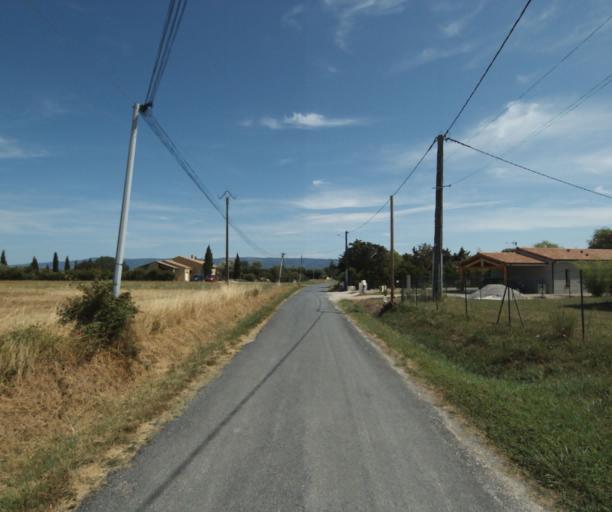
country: FR
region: Midi-Pyrenees
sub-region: Departement du Tarn
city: Puylaurens
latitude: 43.5370
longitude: 2.0128
